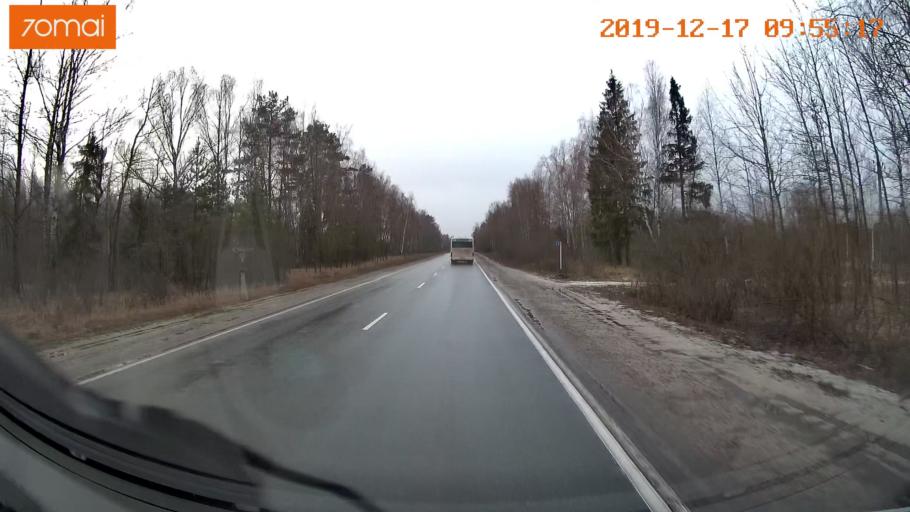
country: RU
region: Vladimir
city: Golovino
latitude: 56.0034
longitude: 40.5672
